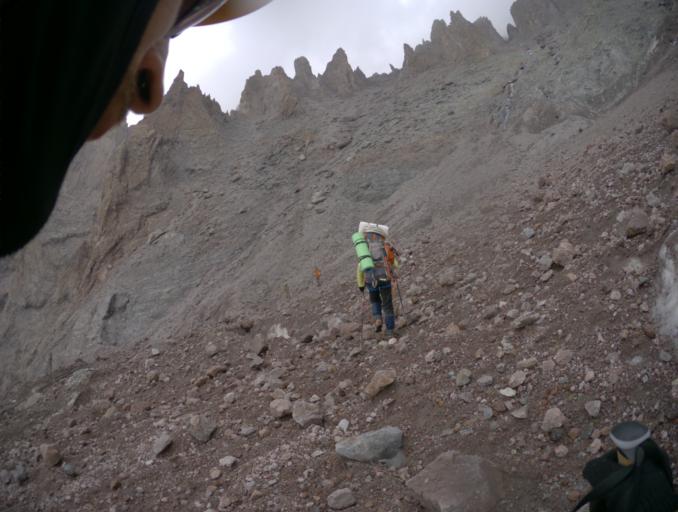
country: RU
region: Kabardino-Balkariya
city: Terskol
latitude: 43.3774
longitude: 42.4038
